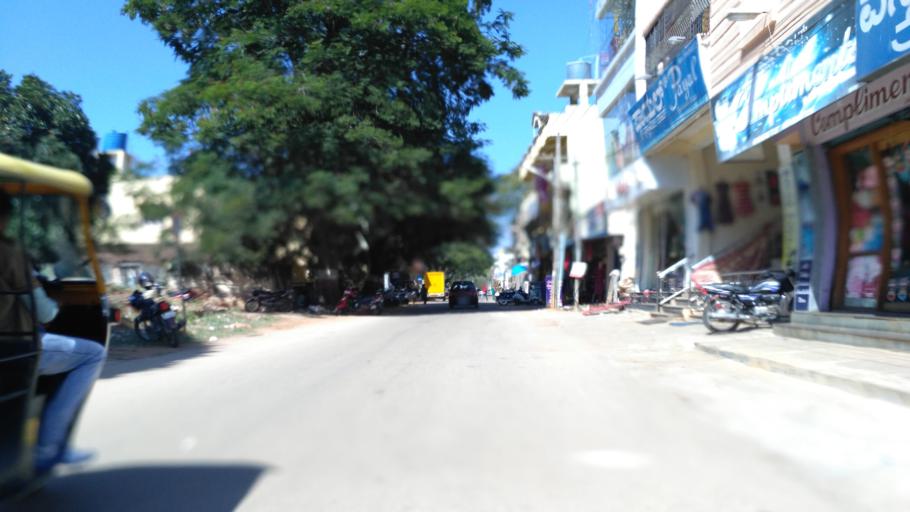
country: IN
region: Karnataka
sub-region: Hassan
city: Hassan
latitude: 13.0088
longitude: 76.1061
